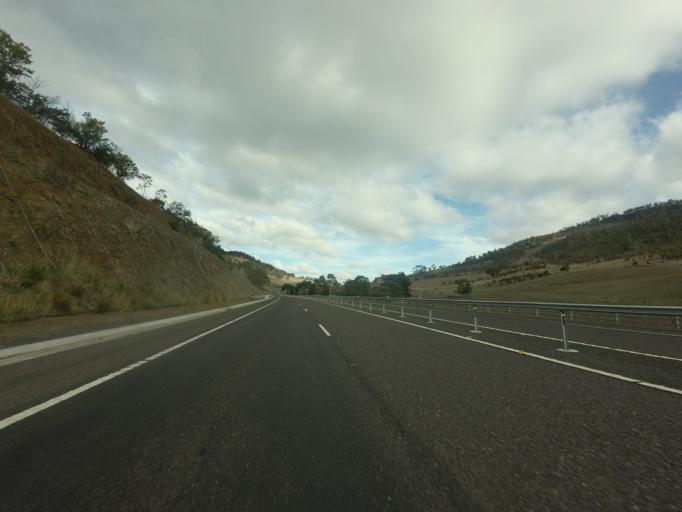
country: AU
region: Tasmania
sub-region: Brighton
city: Bridgewater
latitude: -42.5469
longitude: 147.2075
